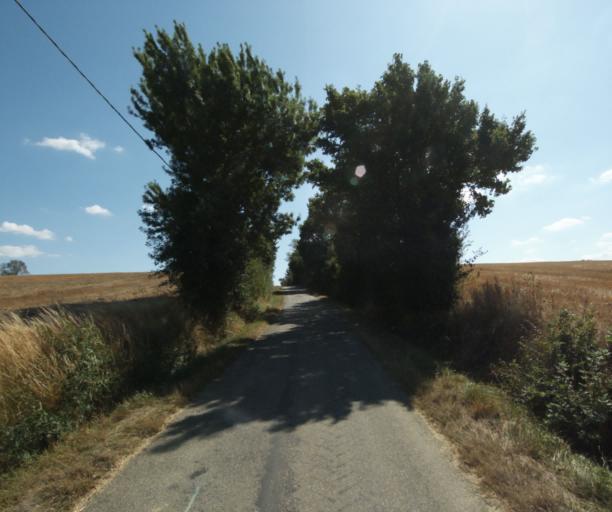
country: FR
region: Midi-Pyrenees
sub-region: Departement de la Haute-Garonne
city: Saint-Felix-Lauragais
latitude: 43.4818
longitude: 1.8970
